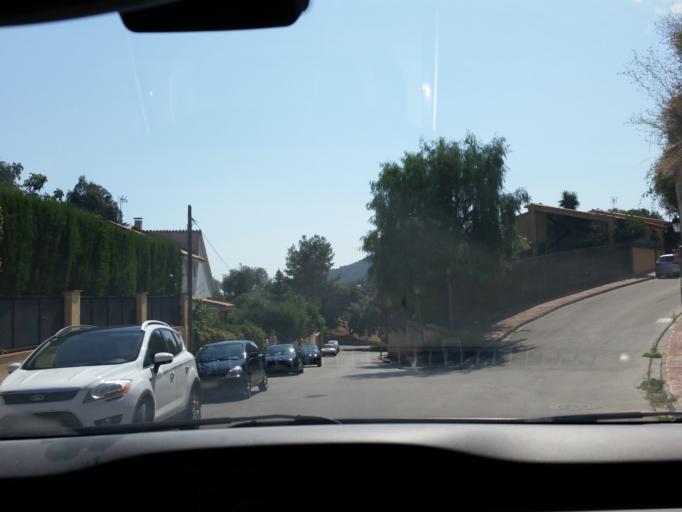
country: ES
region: Catalonia
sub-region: Provincia de Barcelona
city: Cabrils
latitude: 41.5324
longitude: 2.3726
